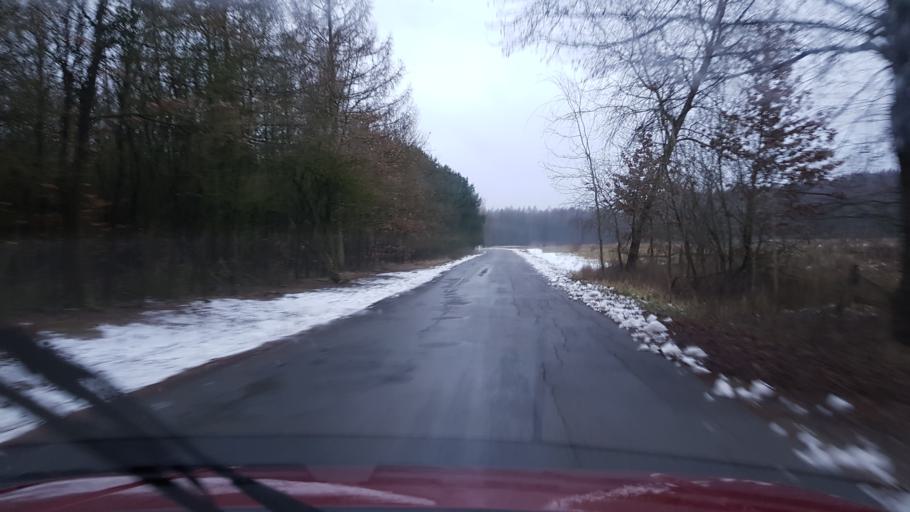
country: PL
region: West Pomeranian Voivodeship
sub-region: Powiat goleniowski
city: Mosty
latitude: 53.4957
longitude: 14.8943
